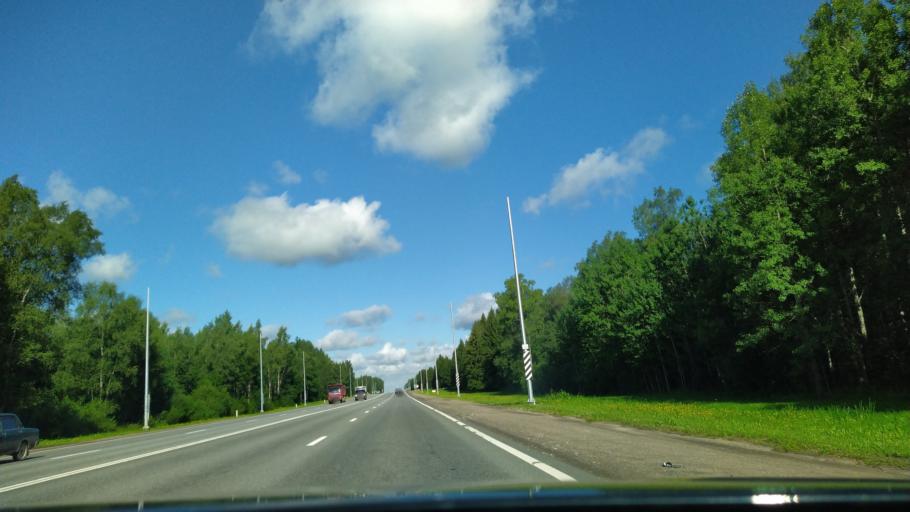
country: RU
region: Leningrad
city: Ul'yanovka
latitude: 59.5875
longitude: 30.7928
